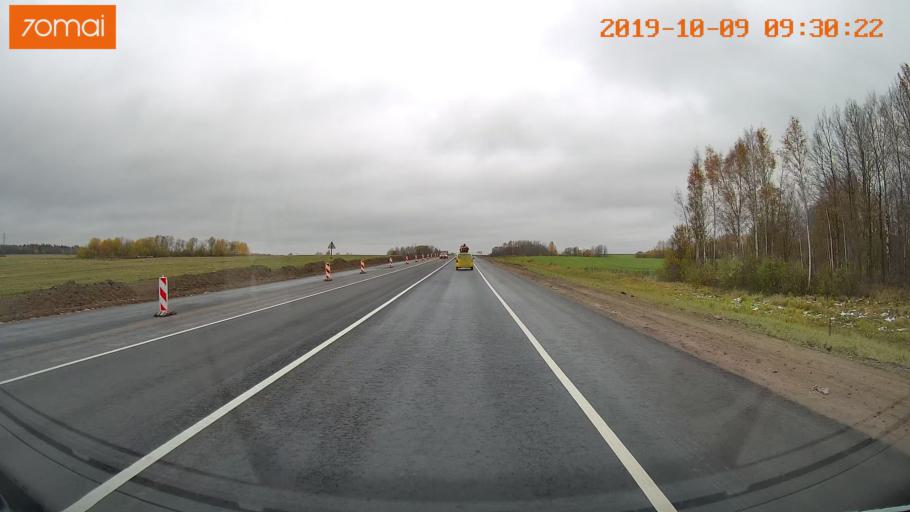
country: RU
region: Vologda
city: Vologda
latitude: 59.1394
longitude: 39.9496
